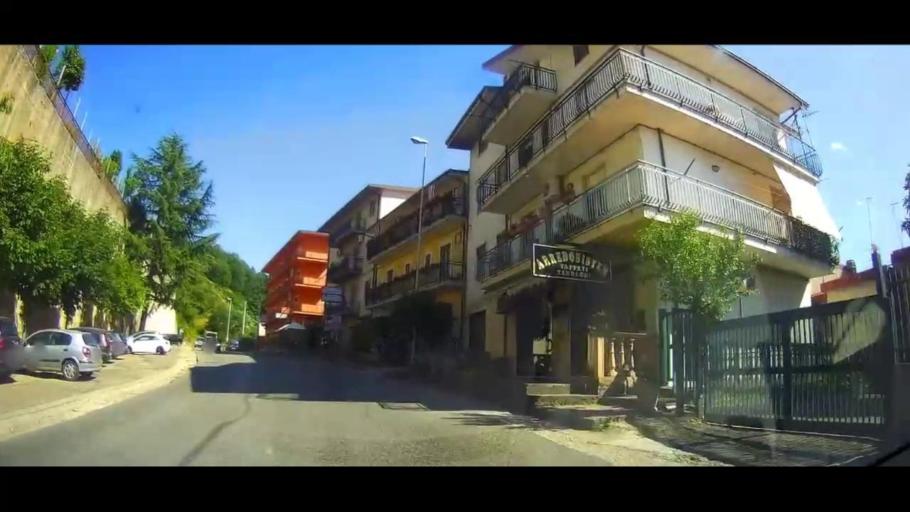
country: IT
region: Calabria
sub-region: Provincia di Cosenza
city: Spezzano della Sila
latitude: 39.3031
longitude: 16.3400
